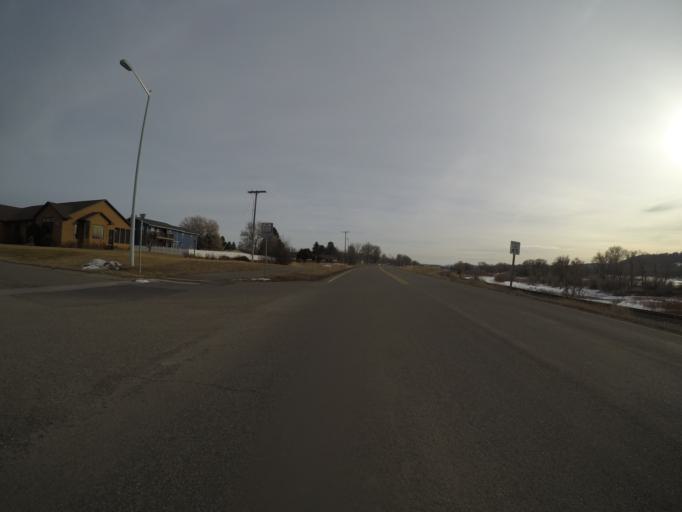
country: US
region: Montana
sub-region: Stillwater County
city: Columbus
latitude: 45.6404
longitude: -109.2668
